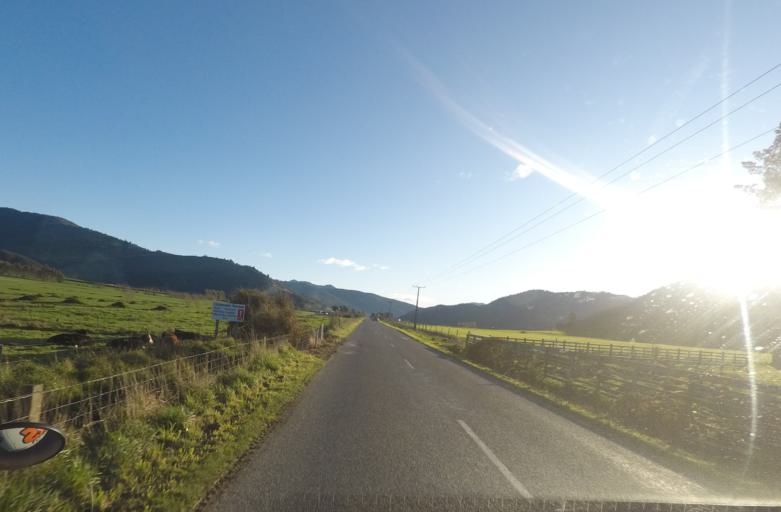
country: NZ
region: Marlborough
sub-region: Marlborough District
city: Picton
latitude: -41.2897
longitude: 173.8787
